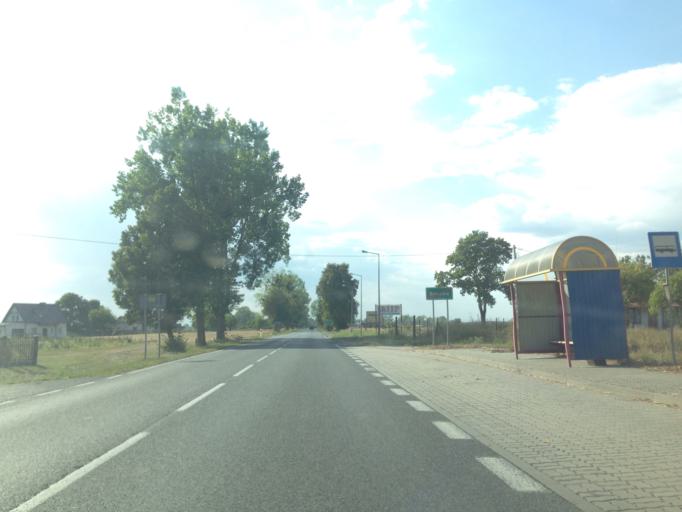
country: PL
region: Kujawsko-Pomorskie
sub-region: Powiat swiecki
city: Bukowiec
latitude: 53.4512
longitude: 18.2305
